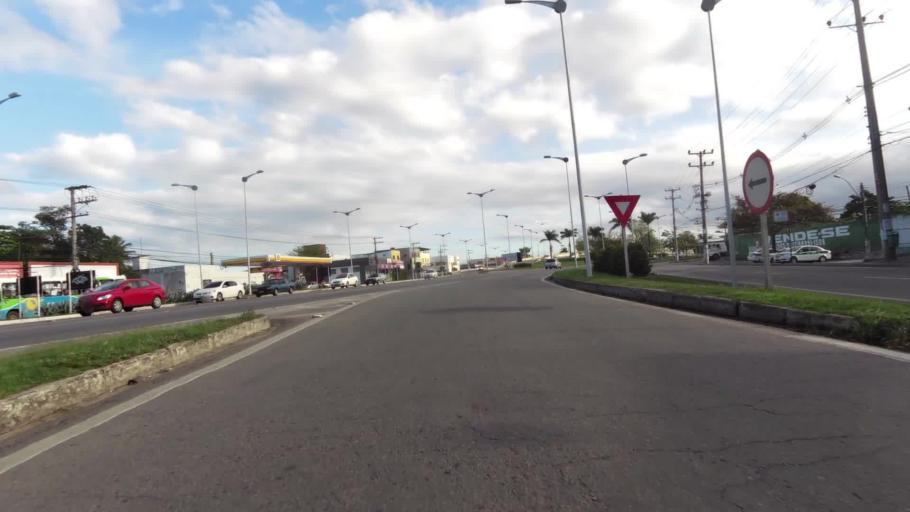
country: BR
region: Espirito Santo
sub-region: Vila Velha
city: Vila Velha
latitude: -20.2311
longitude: -40.2738
